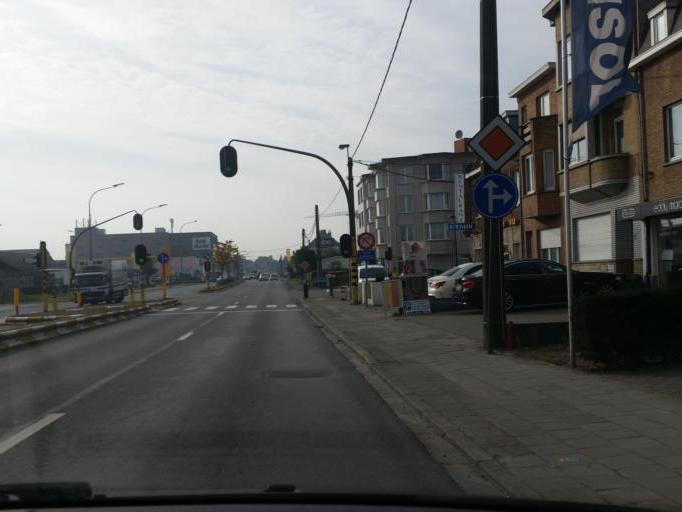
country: BE
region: Flanders
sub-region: Provincie Vlaams-Brabant
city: Drogenbos
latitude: 50.8058
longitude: 4.2887
